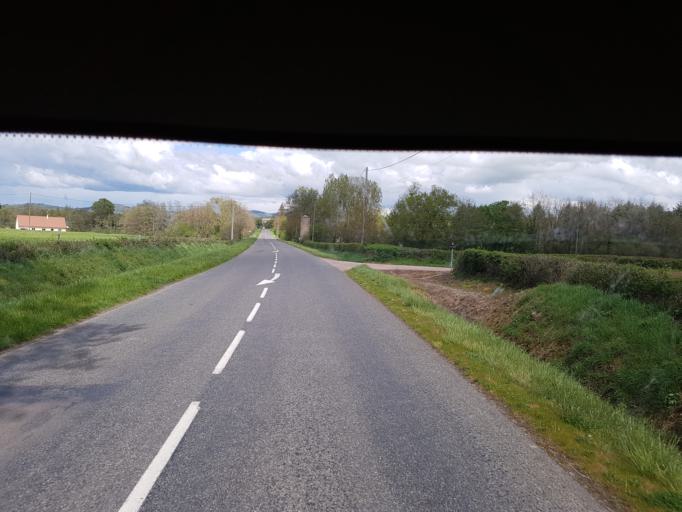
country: FR
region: Bourgogne
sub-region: Departement de Saone-et-Loire
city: Etang-sur-Arroux
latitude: 46.8257
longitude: 4.1760
